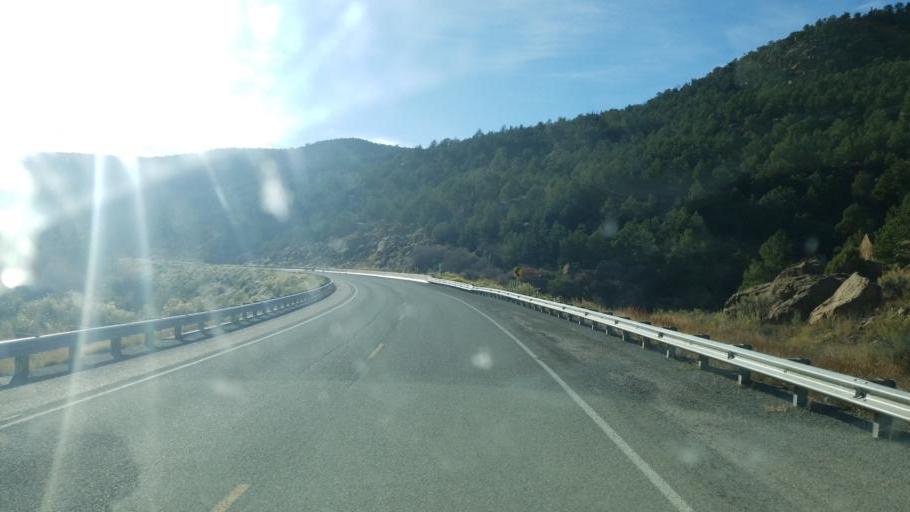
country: US
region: New Mexico
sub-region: Rio Arriba County
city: Navajo
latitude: 36.7346
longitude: -107.2700
